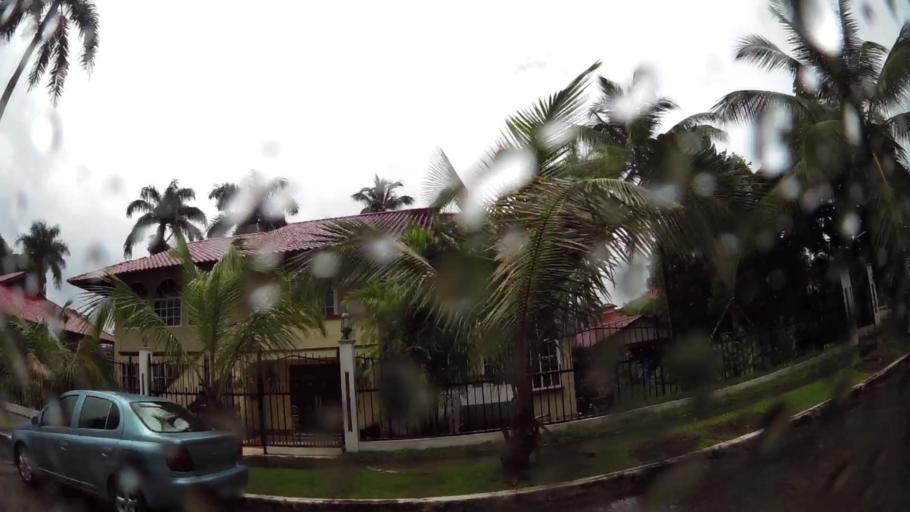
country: PA
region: Panama
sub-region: Distrito de Panama
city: Ancon
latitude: 8.9804
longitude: -79.5595
